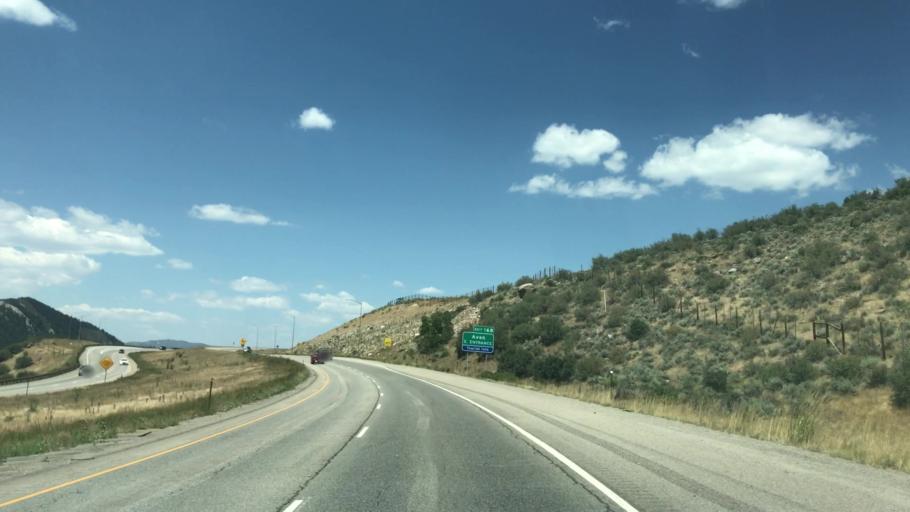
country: US
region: Colorado
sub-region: Eagle County
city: Avon
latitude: 39.6244
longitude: -106.4873
